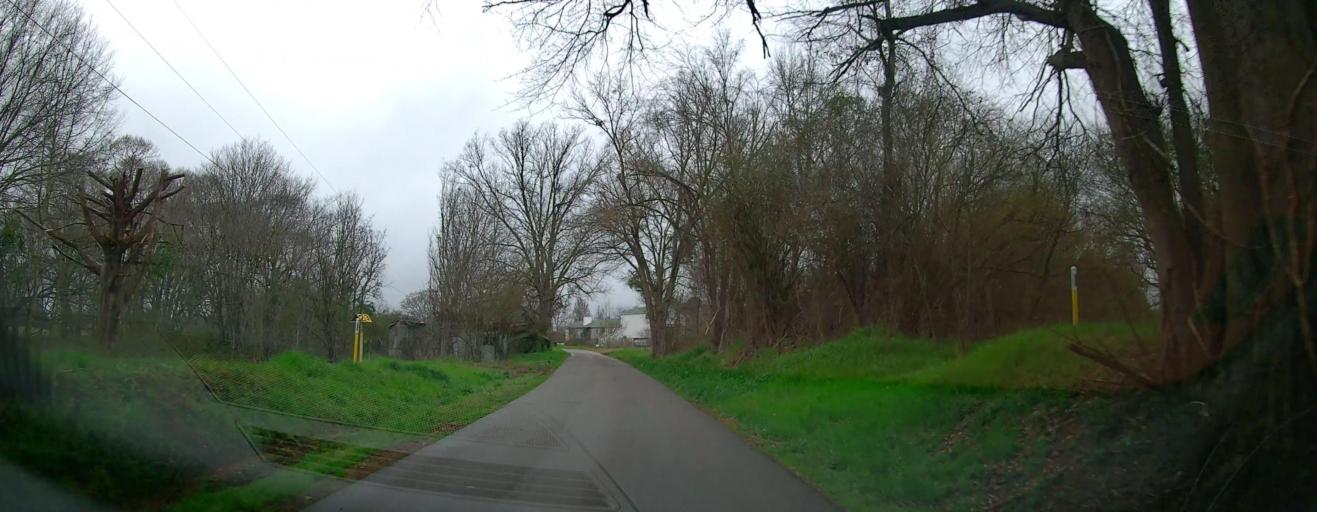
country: US
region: Georgia
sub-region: Monroe County
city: Forsyth
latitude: 33.0533
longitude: -83.8870
